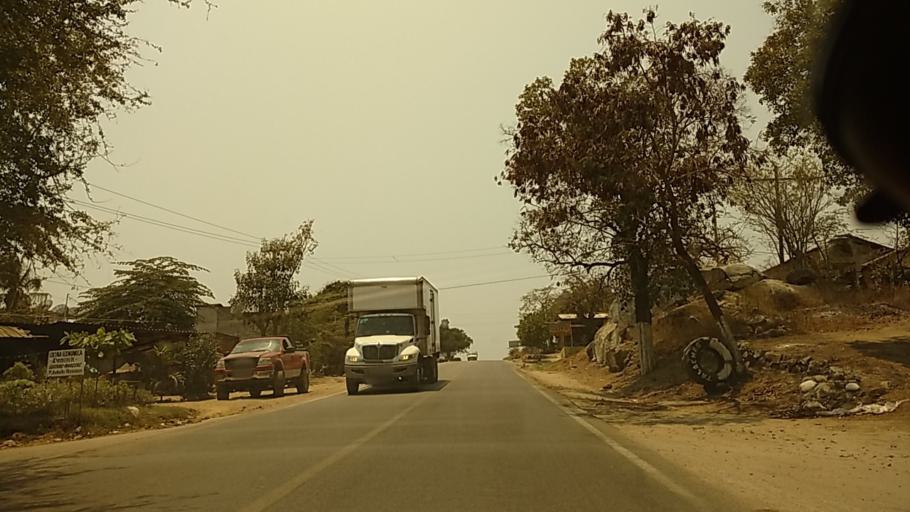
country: MX
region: Guerrero
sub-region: Tecpan de Galeana
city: Villa Rotaria
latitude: 17.2712
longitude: -100.8900
